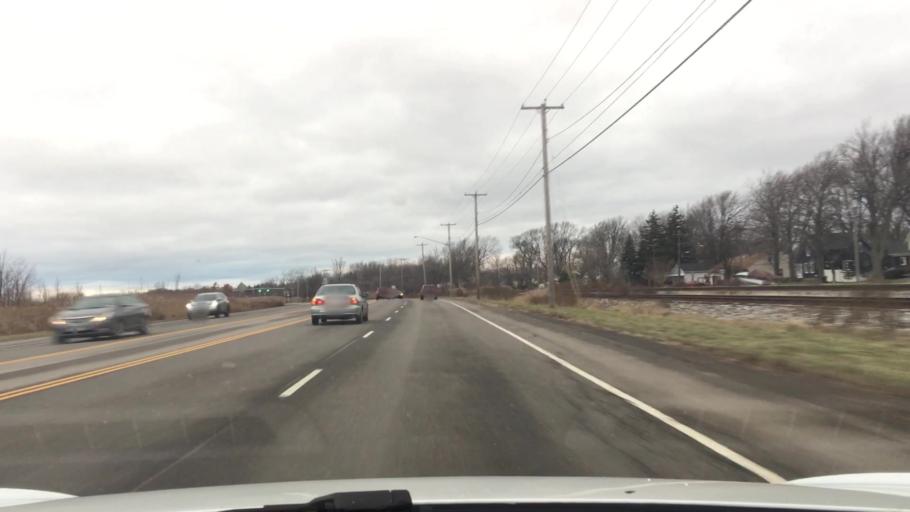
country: US
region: New York
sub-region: Niagara County
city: North Tonawanda
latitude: 43.0489
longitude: -78.8910
